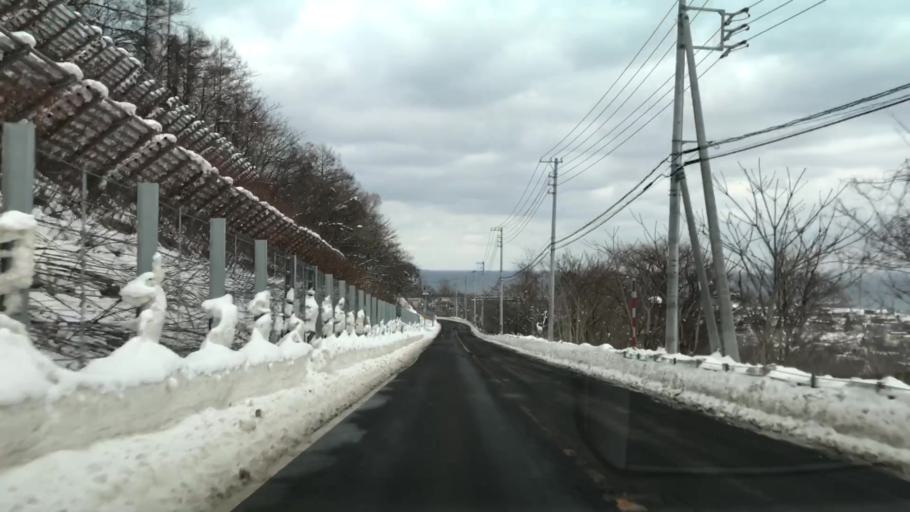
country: JP
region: Hokkaido
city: Yoichi
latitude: 43.2919
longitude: 140.5909
